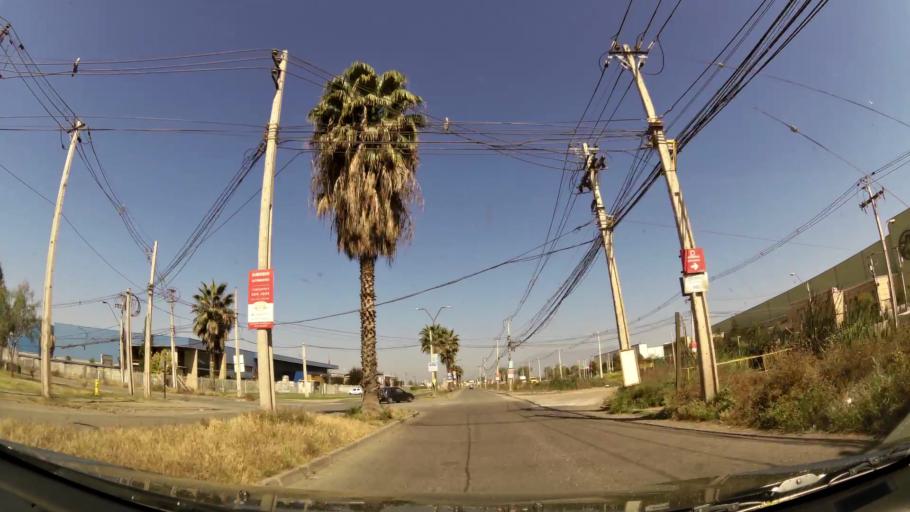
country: CL
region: Santiago Metropolitan
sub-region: Provincia de Chacabuco
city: Chicureo Abajo
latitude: -33.3217
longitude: -70.7379
